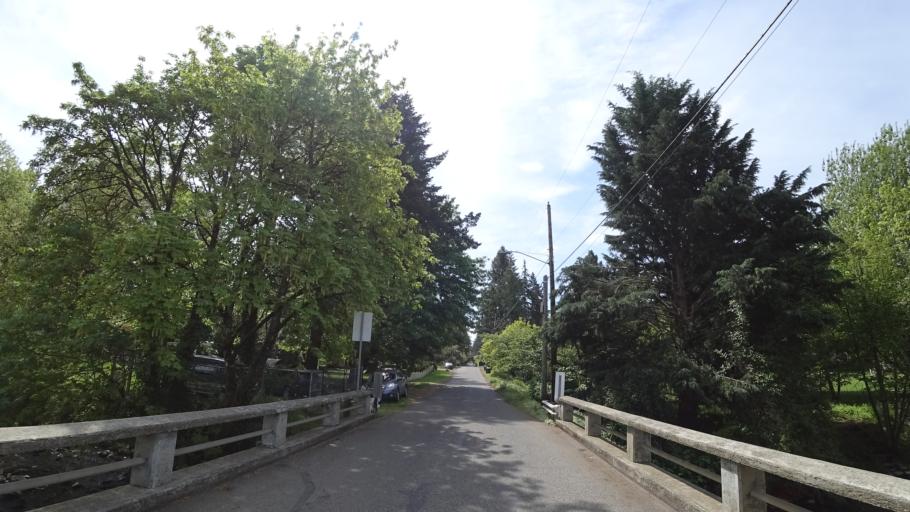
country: US
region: Oregon
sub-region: Clackamas County
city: Milwaukie
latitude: 45.4559
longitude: -122.6009
